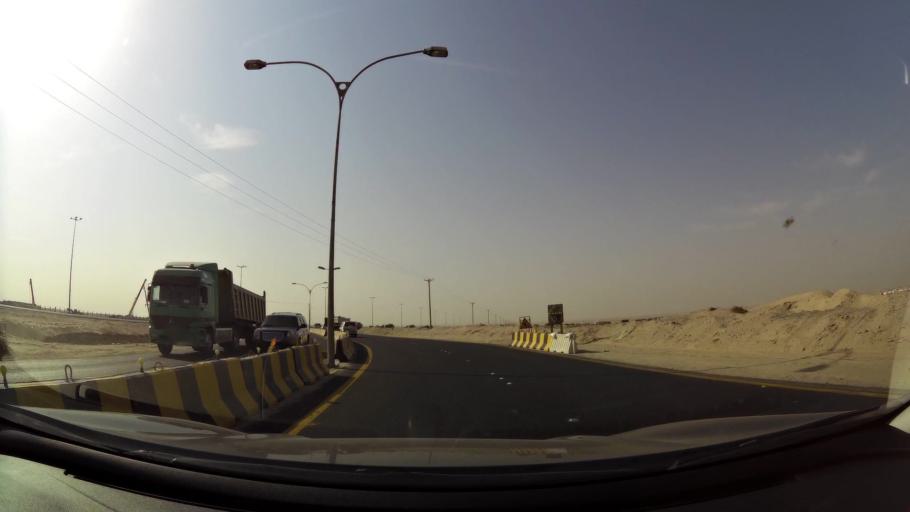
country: KW
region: Al Ahmadi
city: Al Ahmadi
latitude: 28.8881
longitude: 48.0835
